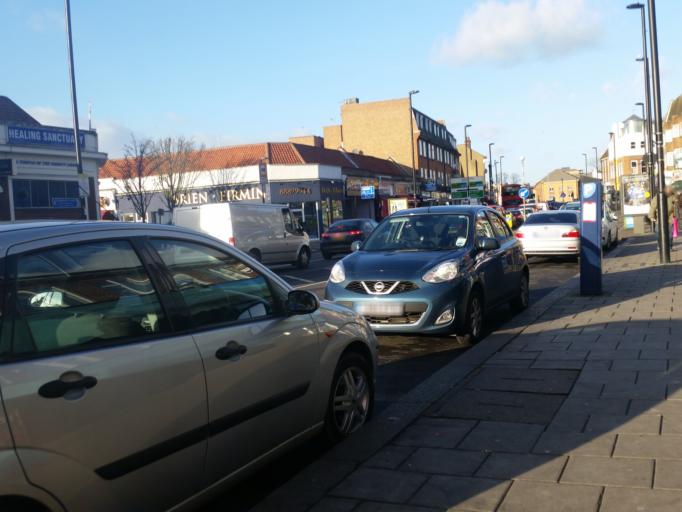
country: GB
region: England
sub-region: Greater London
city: Wood Green
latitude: 51.6106
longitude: -0.1095
